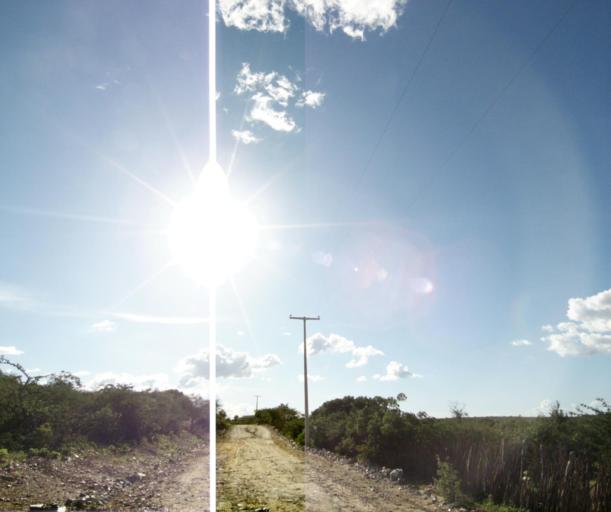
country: BR
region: Bahia
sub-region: Tanhacu
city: Tanhacu
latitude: -14.1824
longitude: -41.0097
